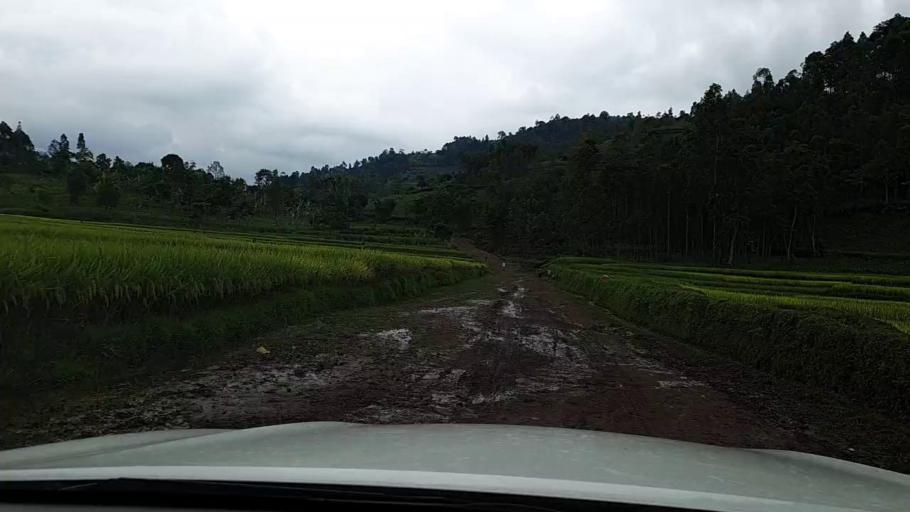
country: RW
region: Western Province
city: Cyangugu
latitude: -2.5643
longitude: 29.0355
